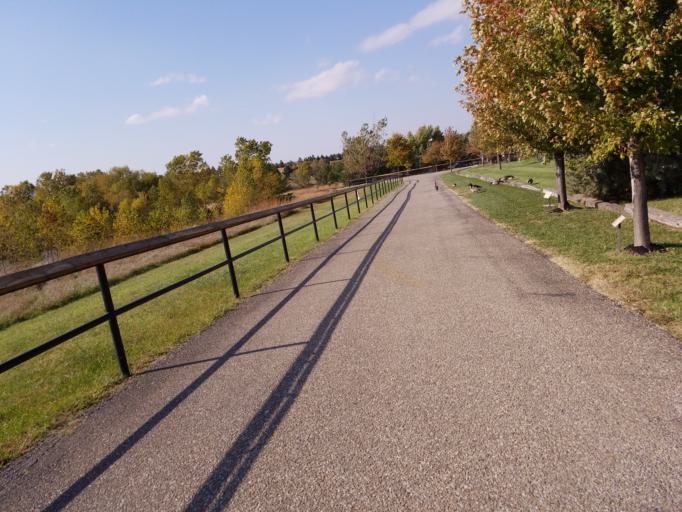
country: US
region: Kansas
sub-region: Saline County
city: Salina
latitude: 38.8510
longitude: -97.7641
